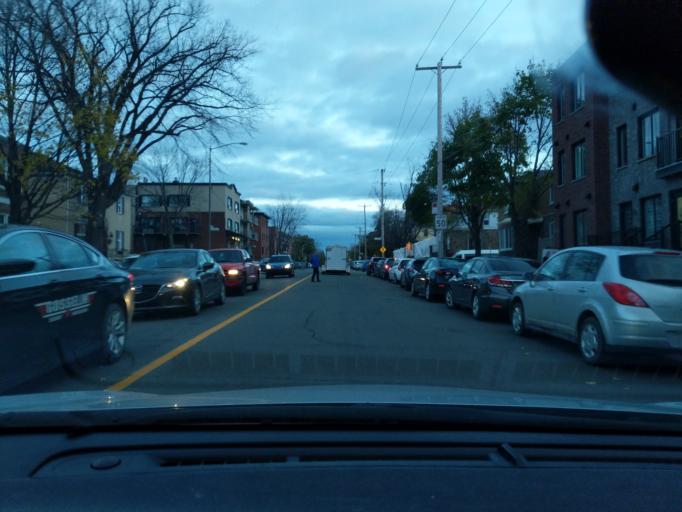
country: CA
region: Quebec
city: Quebec
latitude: 46.7938
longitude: -71.2557
